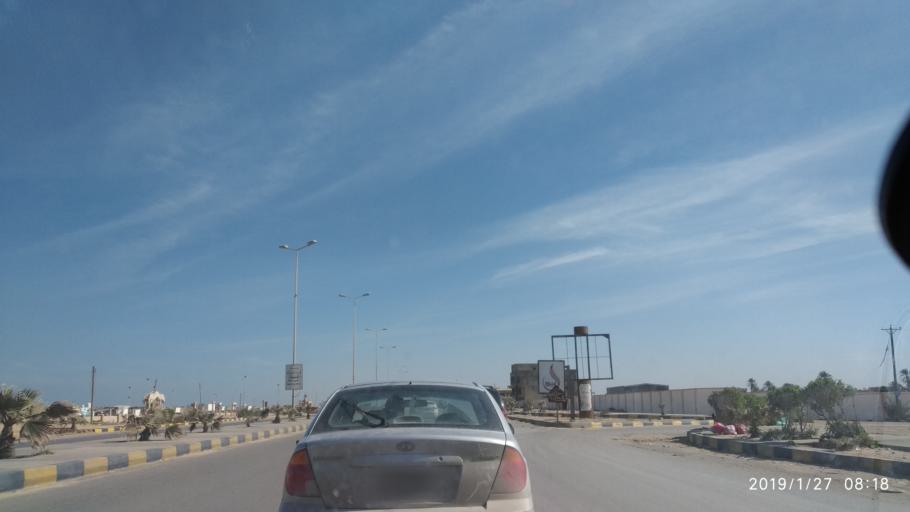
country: LY
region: Tripoli
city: Tagiura
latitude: 32.8953
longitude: 13.3290
